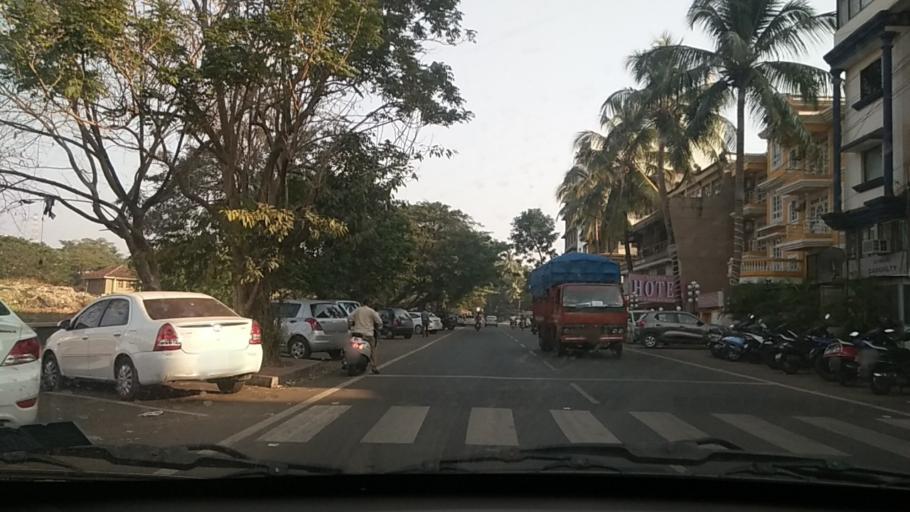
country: IN
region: Goa
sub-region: North Goa
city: Panaji
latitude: 15.4887
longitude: 73.8155
